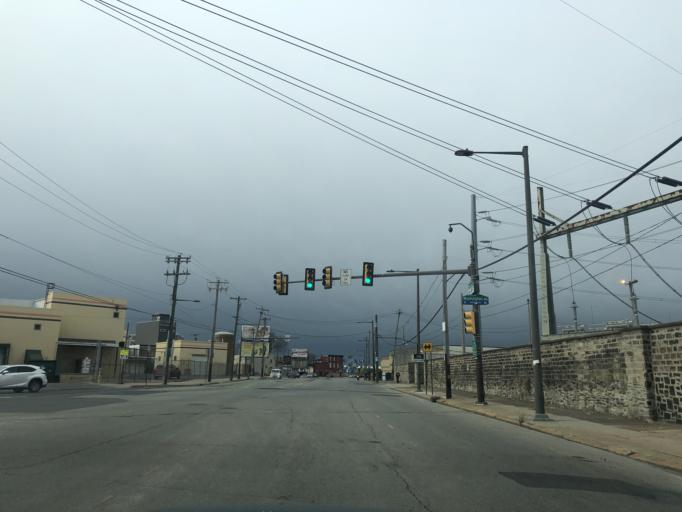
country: US
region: Pennsylvania
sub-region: Philadelphia County
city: Philadelphia
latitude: 39.9407
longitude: -75.1871
